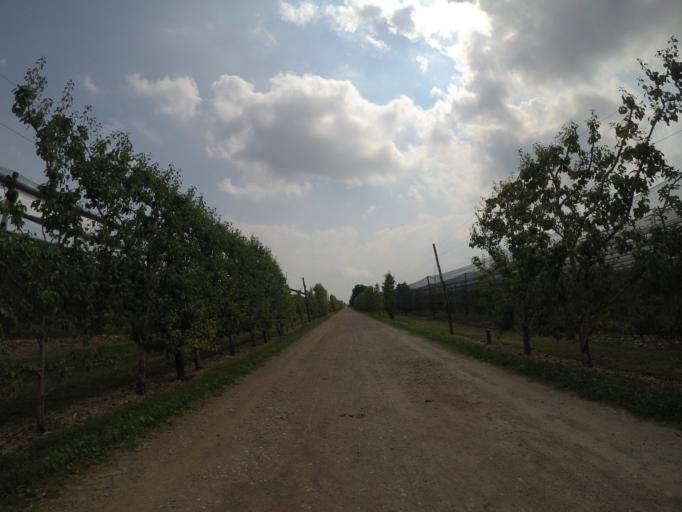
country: IT
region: Friuli Venezia Giulia
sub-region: Provincia di Udine
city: Sedegliano
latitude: 45.9946
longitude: 13.0108
